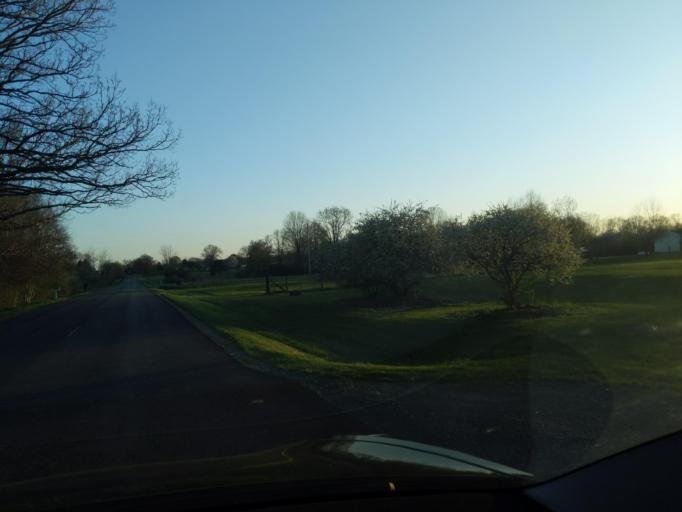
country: US
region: Michigan
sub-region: Ingham County
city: Stockbridge
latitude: 42.4935
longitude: -84.2880
